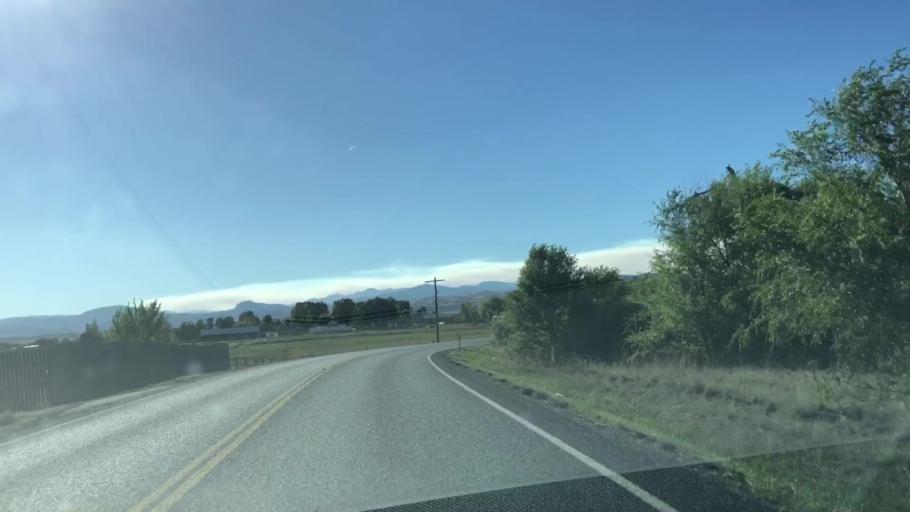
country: US
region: Colorado
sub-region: Larimer County
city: Loveland
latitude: 40.4609
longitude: -105.0523
